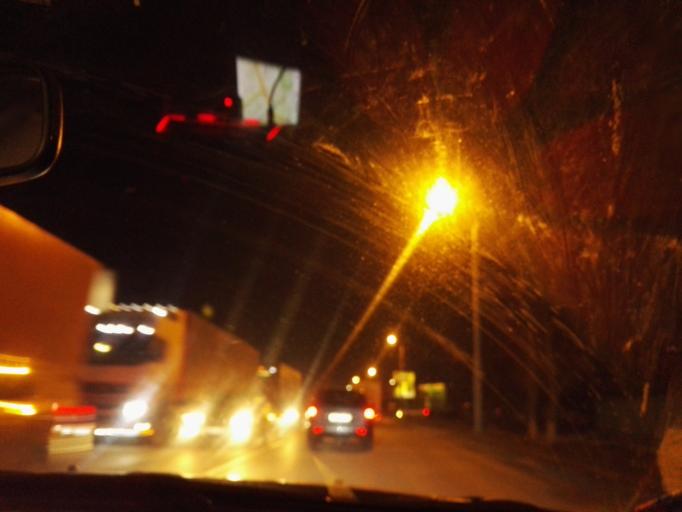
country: RU
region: Tula
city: Tula
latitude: 54.1626
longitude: 37.6379
